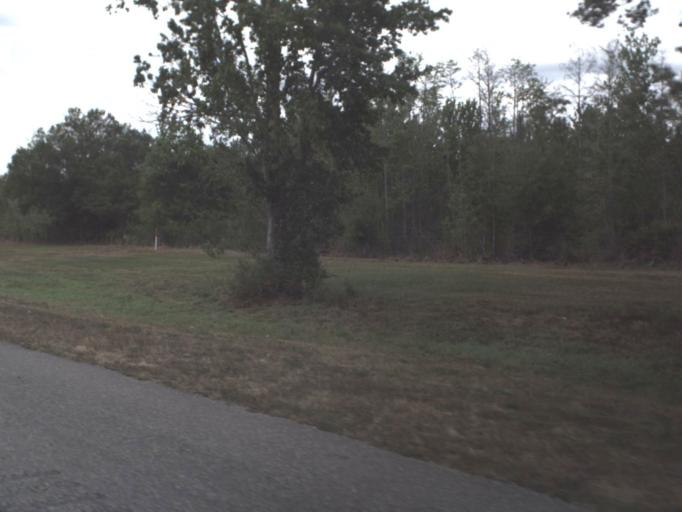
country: US
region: Florida
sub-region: Orange County
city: Wedgefield
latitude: 28.4518
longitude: -81.0880
